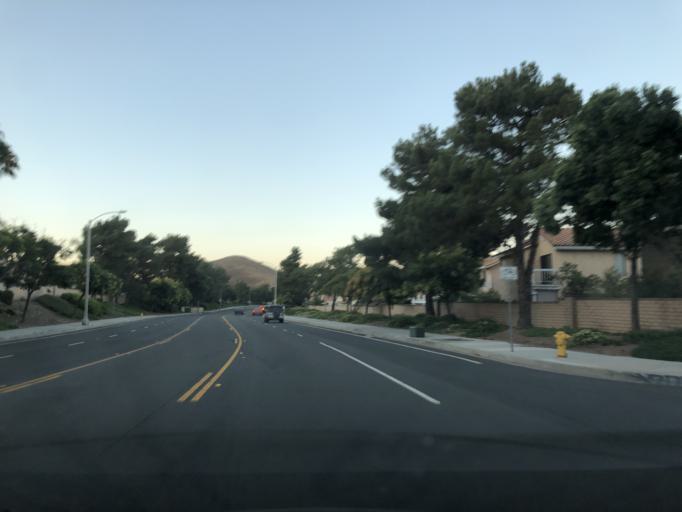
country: US
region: California
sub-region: Riverside County
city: Home Gardens
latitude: 33.8976
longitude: -117.5095
